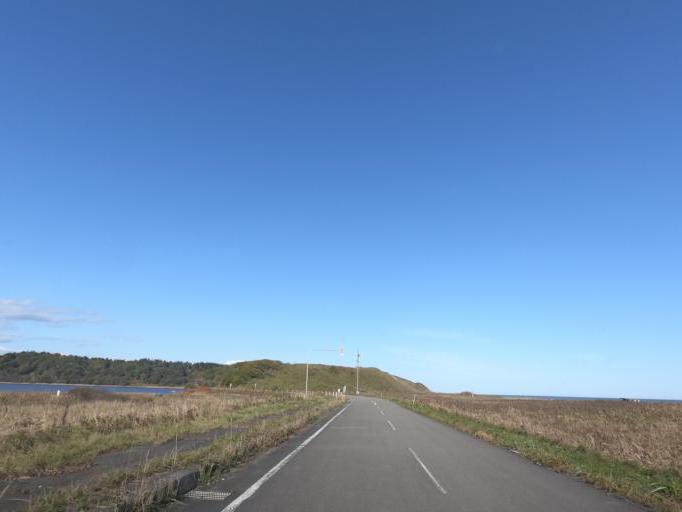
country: JP
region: Hokkaido
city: Obihiro
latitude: 42.5993
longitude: 143.5490
